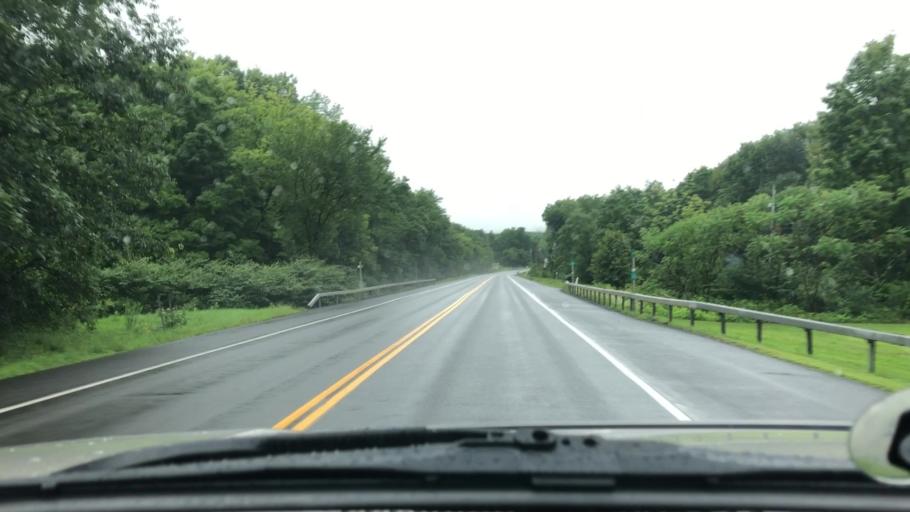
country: US
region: New York
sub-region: Greene County
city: Cairo
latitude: 42.3206
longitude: -74.0850
